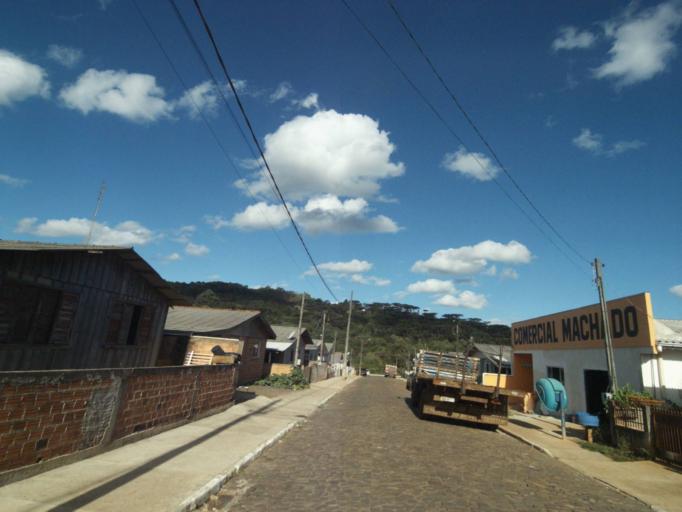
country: BR
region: Parana
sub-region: Uniao Da Vitoria
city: Uniao da Vitoria
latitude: -26.1607
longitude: -51.5333
